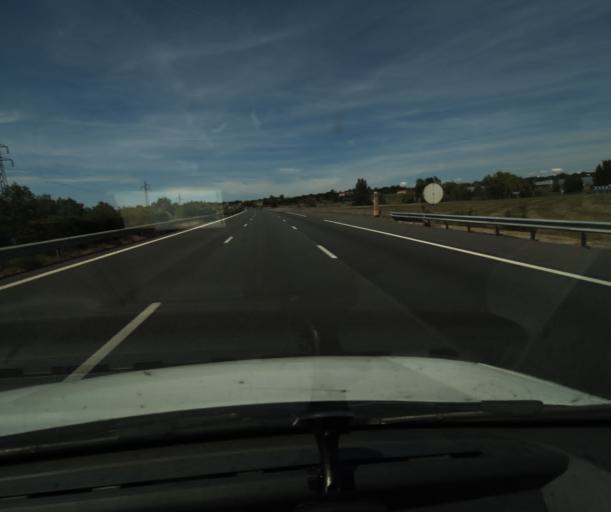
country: FR
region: Midi-Pyrenees
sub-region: Departement de la Haute-Garonne
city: Saint-Sauveur
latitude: 43.7652
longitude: 1.3856
